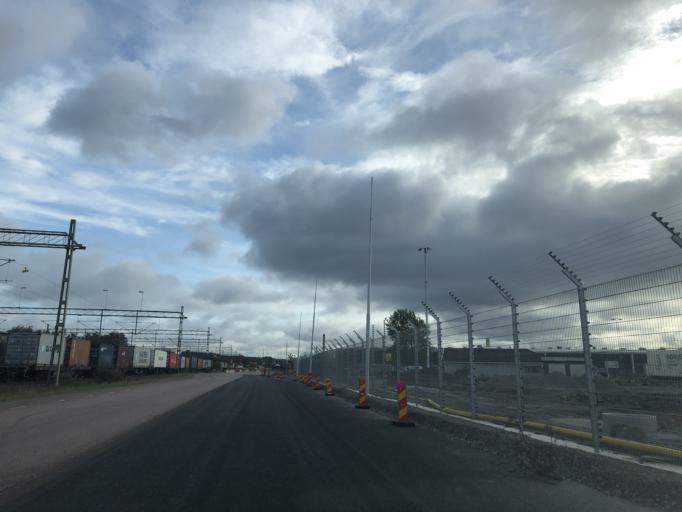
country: SE
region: Vaestra Goetaland
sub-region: Goteborg
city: Majorna
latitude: 57.6972
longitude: 11.8485
